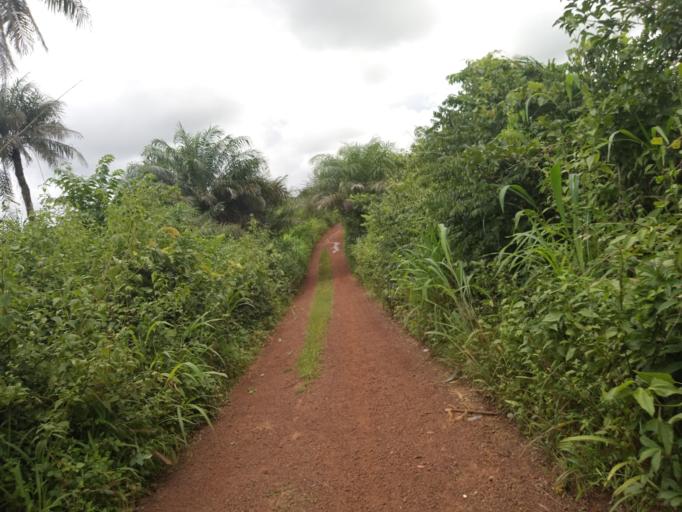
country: SL
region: Northern Province
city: Kamakwie
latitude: 9.4805
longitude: -12.2496
